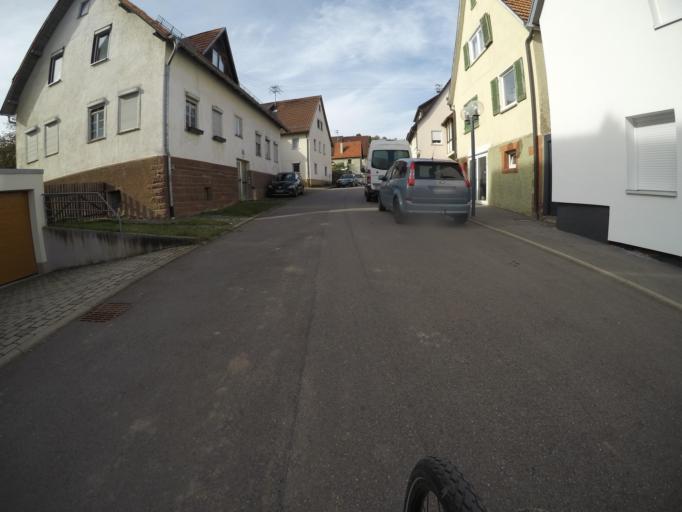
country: DE
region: Baden-Wuerttemberg
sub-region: Karlsruhe Region
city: Simmozheim
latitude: 48.7499
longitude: 8.8102
